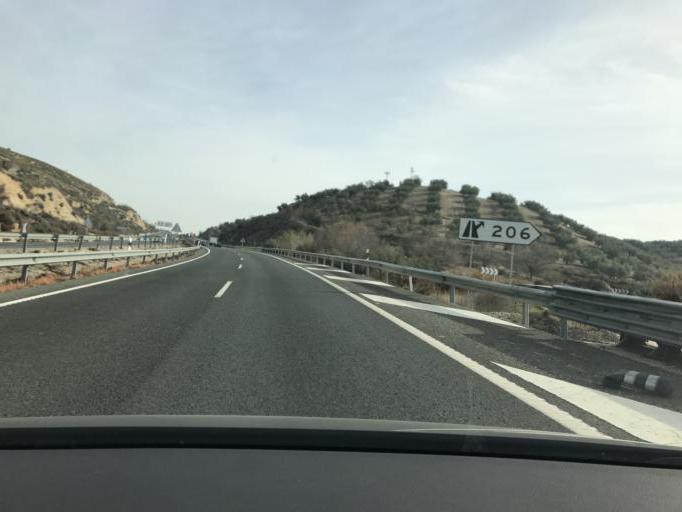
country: ES
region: Andalusia
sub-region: Provincia de Granada
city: Villanueva de Mesia
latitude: 37.1928
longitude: -3.9984
